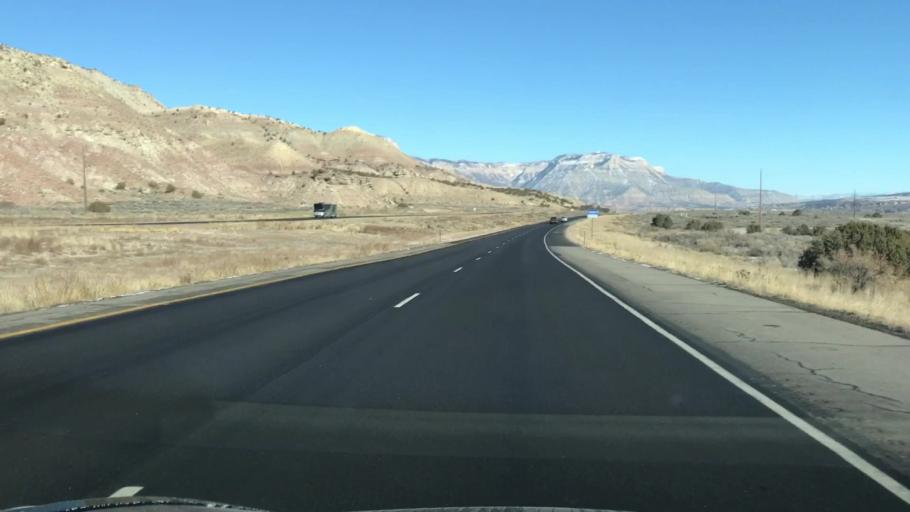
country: US
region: Colorado
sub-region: Garfield County
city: Parachute
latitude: 39.4172
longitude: -108.0908
